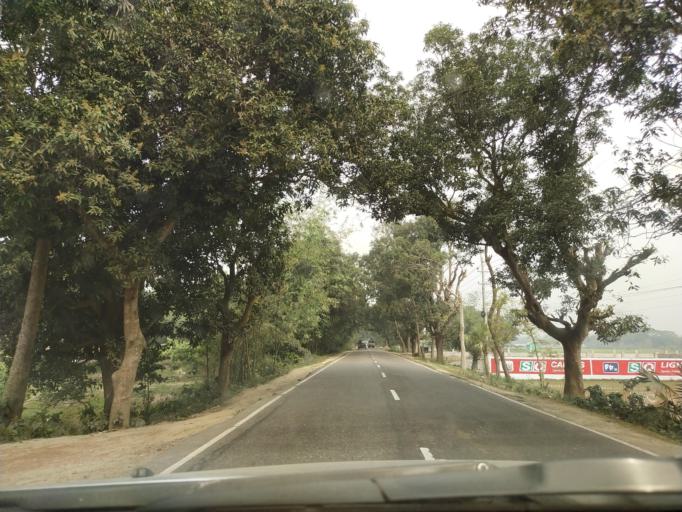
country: BD
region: Dhaka
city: Narsingdi
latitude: 24.0023
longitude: 90.7375
